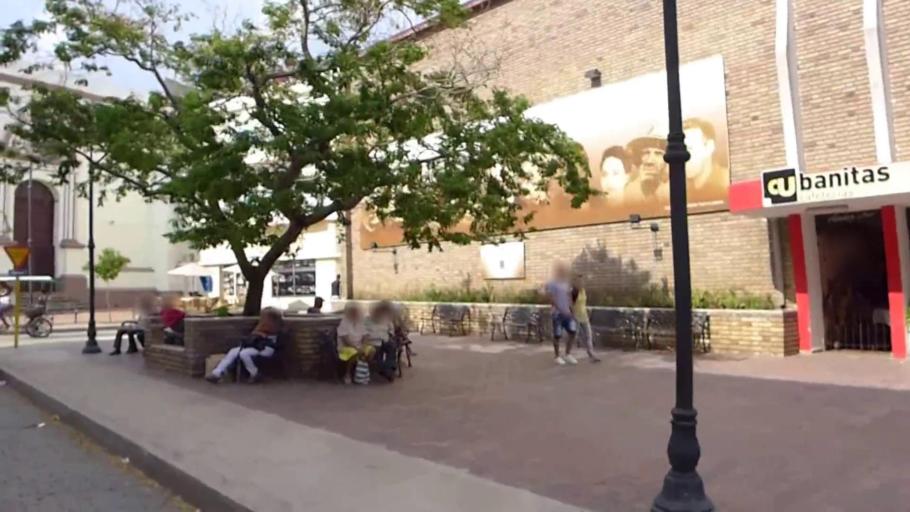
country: CU
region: Camaguey
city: Camaguey
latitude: 21.3822
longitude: -77.9185
